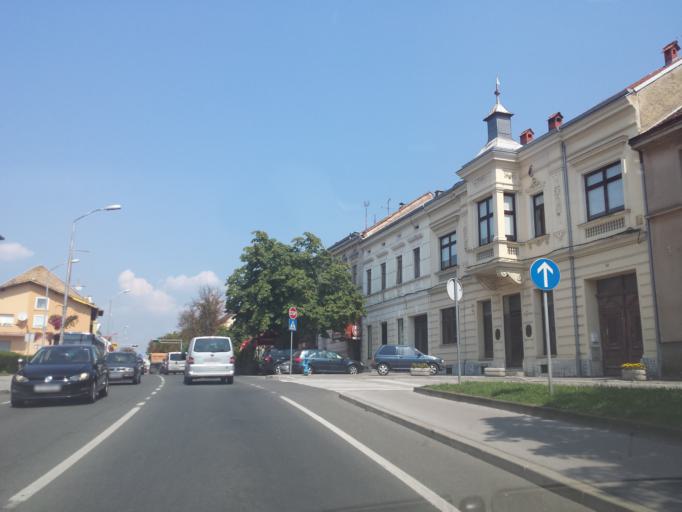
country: HR
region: Zagrebacka
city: Jastrebarsko
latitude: 45.6727
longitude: 15.6516
